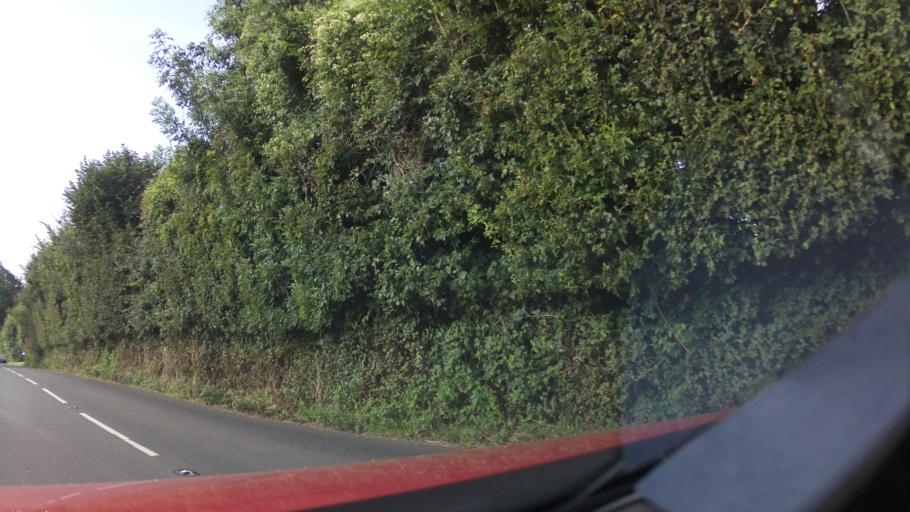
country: GB
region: England
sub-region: Bath and North East Somerset
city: Chew Magna
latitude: 51.3473
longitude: -2.6340
